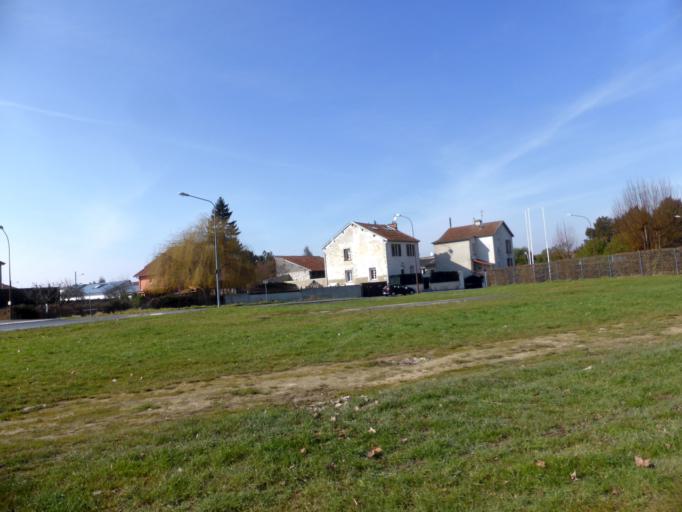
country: FR
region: Champagne-Ardenne
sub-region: Departement de la Marne
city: Chalons-en-Champagne
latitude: 48.9612
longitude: 4.3572
